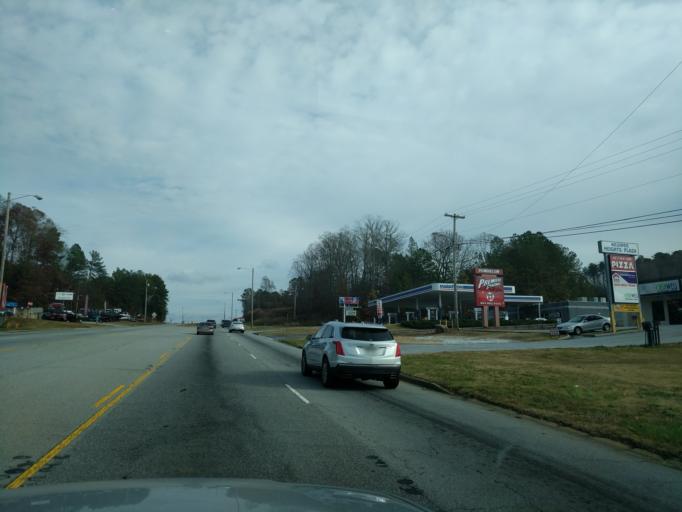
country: US
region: South Carolina
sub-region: Oconee County
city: Seneca
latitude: 34.6964
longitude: -82.9684
